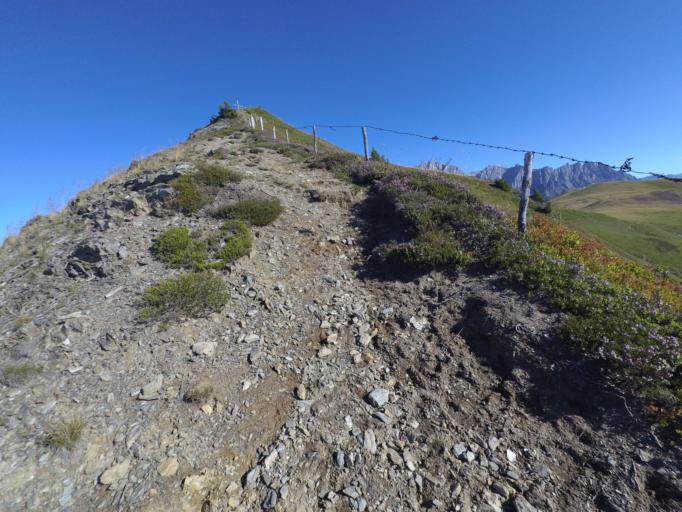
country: AT
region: Salzburg
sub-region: Politischer Bezirk Sankt Johann im Pongau
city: Goldegg
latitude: 47.3649
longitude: 13.0699
